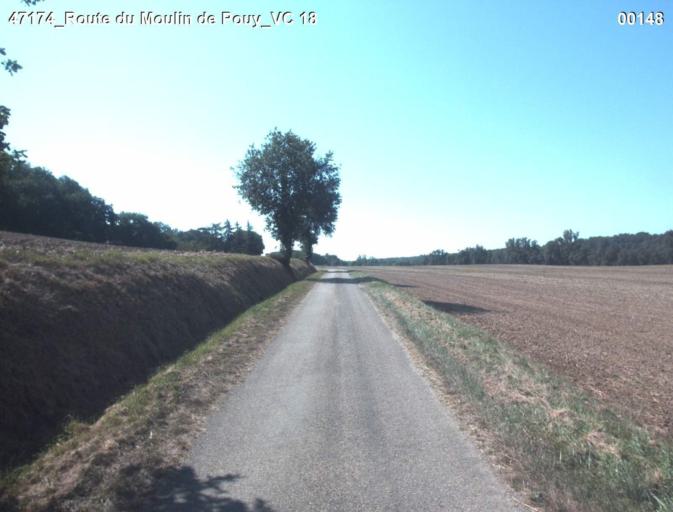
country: FR
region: Aquitaine
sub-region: Departement du Lot-et-Garonne
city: Mezin
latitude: 44.0628
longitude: 0.3191
